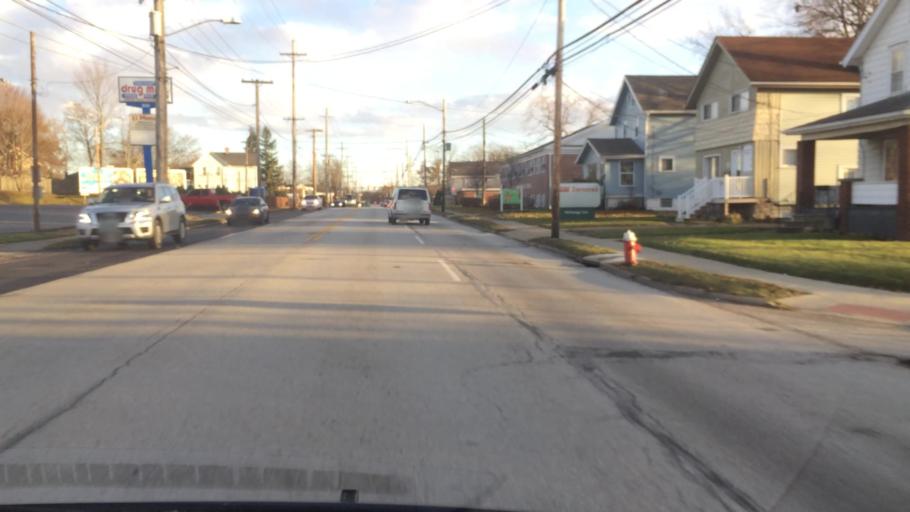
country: US
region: Ohio
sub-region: Summit County
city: Cuyahoga Falls
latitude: 41.1398
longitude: -81.4922
